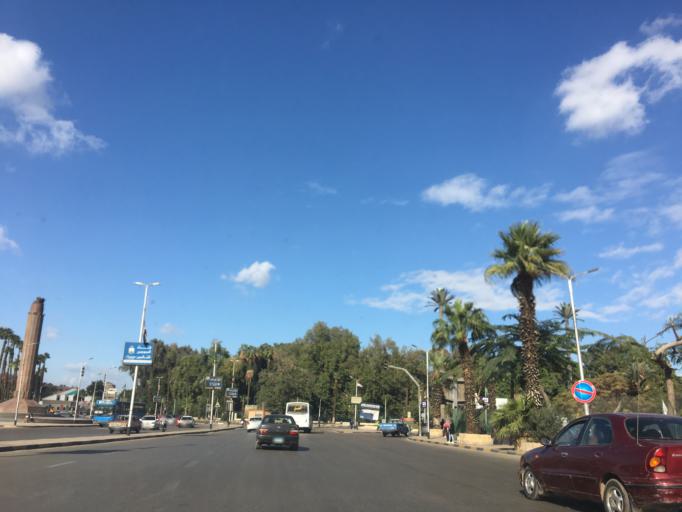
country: EG
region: Al Jizah
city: Al Jizah
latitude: 30.0268
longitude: 31.2109
